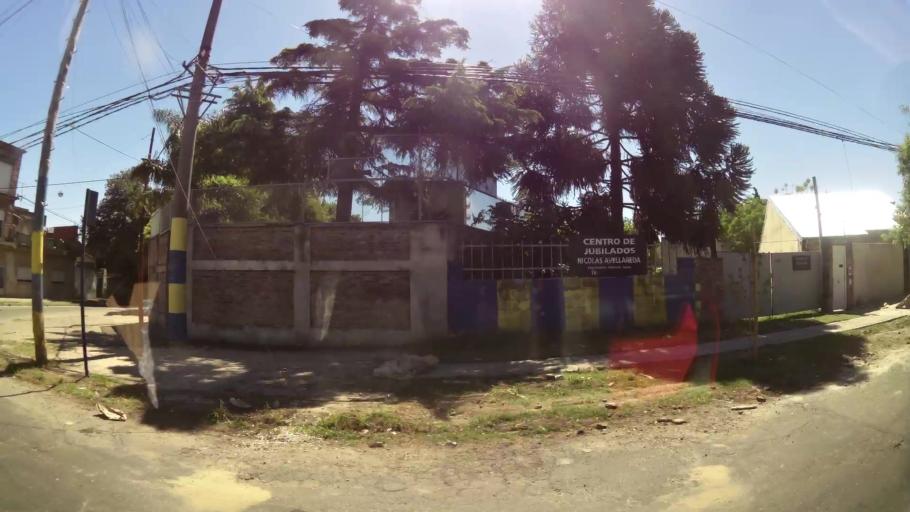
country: AR
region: Santa Fe
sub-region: Departamento de Rosario
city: Rosario
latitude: -32.9350
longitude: -60.6810
